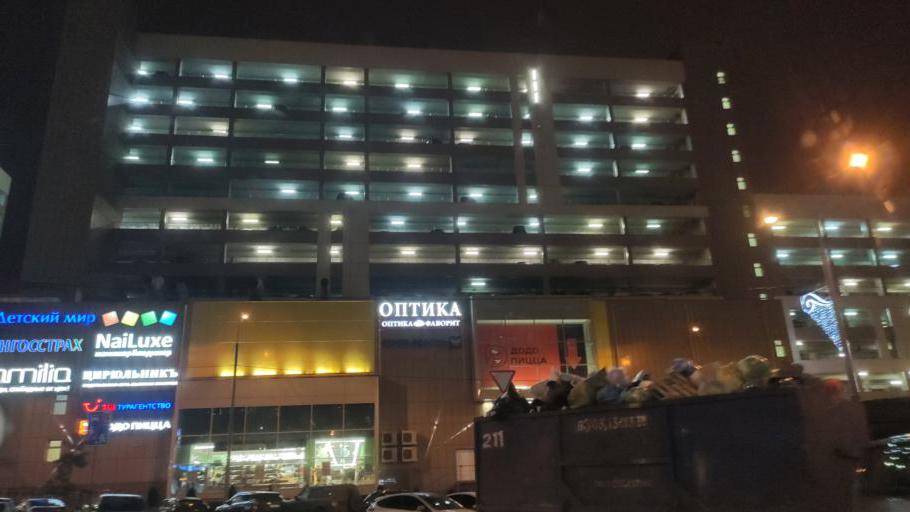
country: RU
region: Moskovskaya
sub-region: Leninskiy Rayon
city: Vnukovo
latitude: 55.6252
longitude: 37.3080
